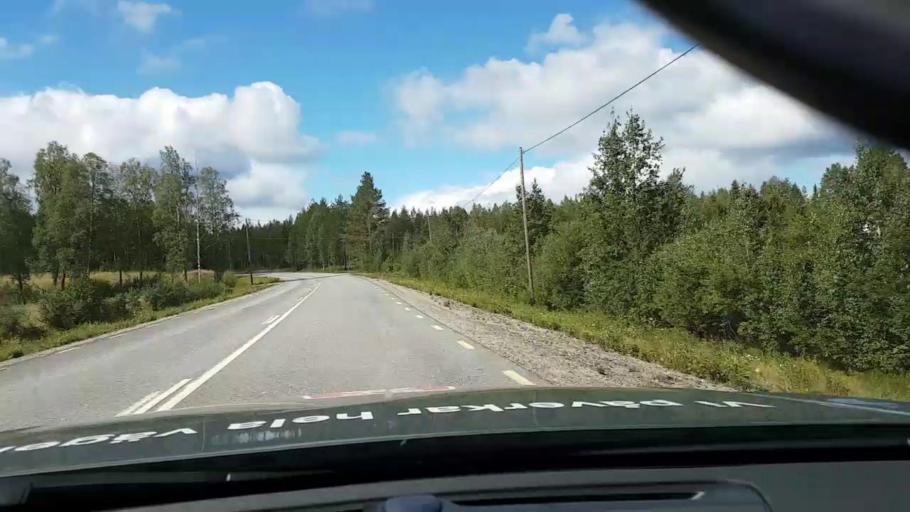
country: SE
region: Vaesternorrland
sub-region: OErnskoeldsviks Kommun
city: Bredbyn
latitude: 63.5296
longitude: 17.9859
